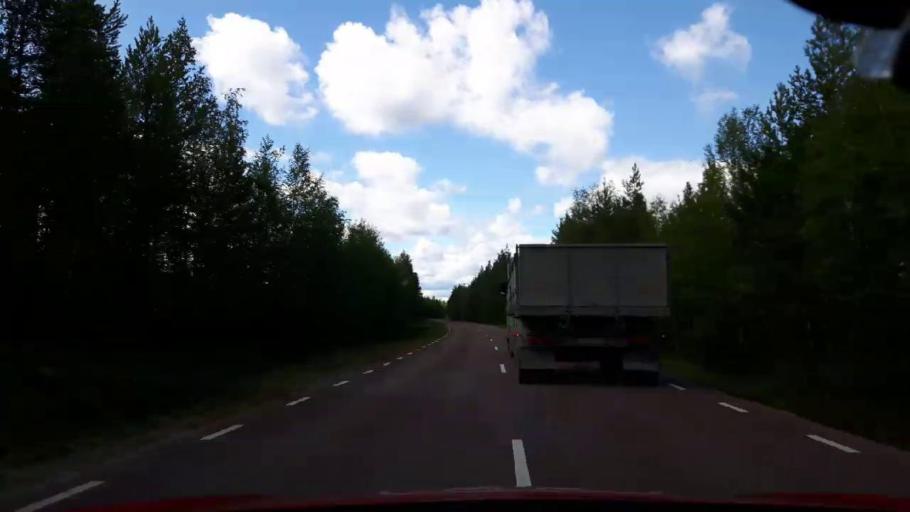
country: SE
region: Jaemtland
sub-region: Harjedalens Kommun
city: Sveg
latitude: 62.0034
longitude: 14.2867
